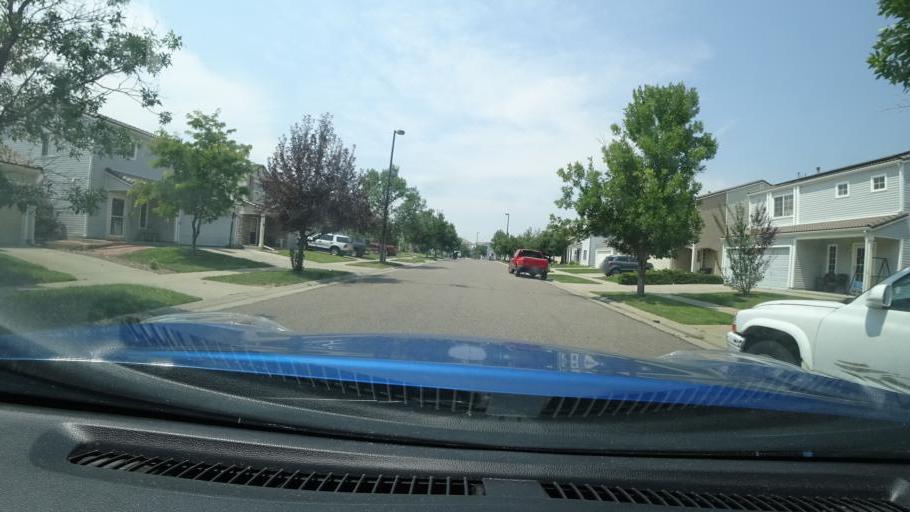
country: US
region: Colorado
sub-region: Adams County
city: Aurora
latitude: 39.7719
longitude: -104.7684
